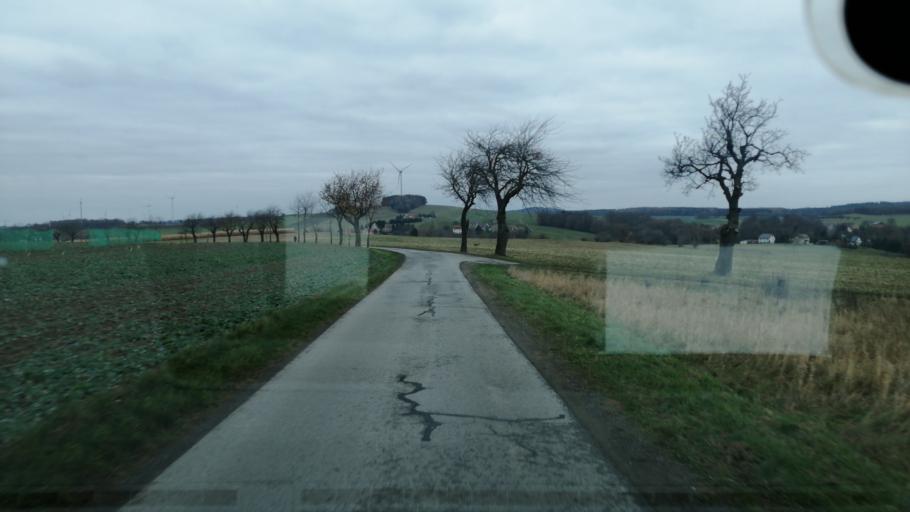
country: DE
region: Saxony
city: Bernstadt
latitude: 51.0570
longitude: 14.7986
